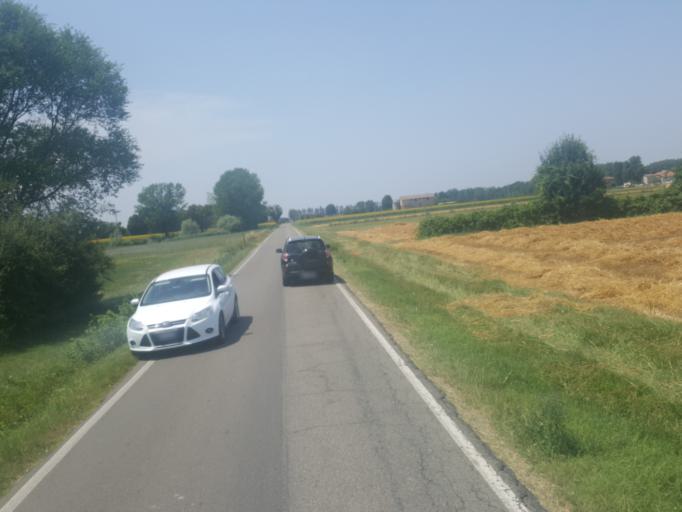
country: IT
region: Emilia-Romagna
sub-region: Provincia di Modena
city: Castelfranco Emilia
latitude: 44.6221
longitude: 11.0482
